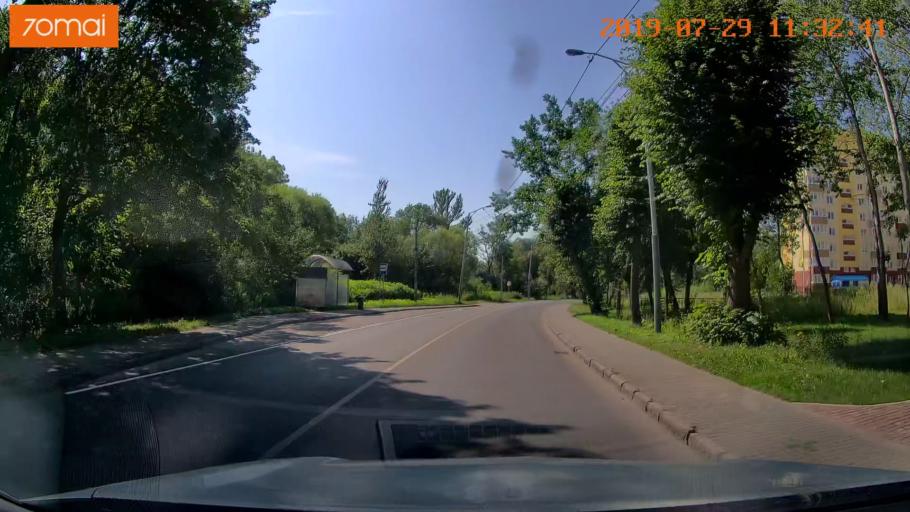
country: RU
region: Kaliningrad
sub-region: Gorod Kaliningrad
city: Kaliningrad
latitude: 54.6706
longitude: 20.5455
